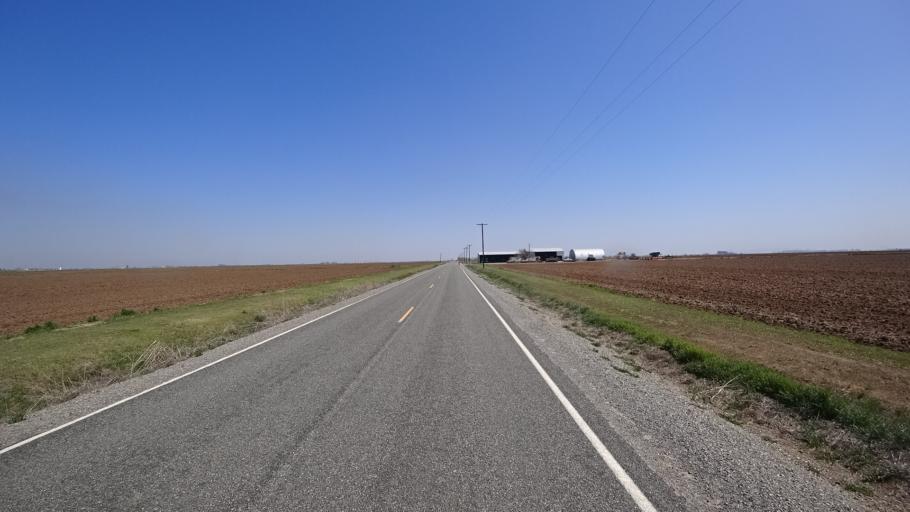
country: US
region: California
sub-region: Glenn County
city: Willows
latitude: 39.4948
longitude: -122.1718
